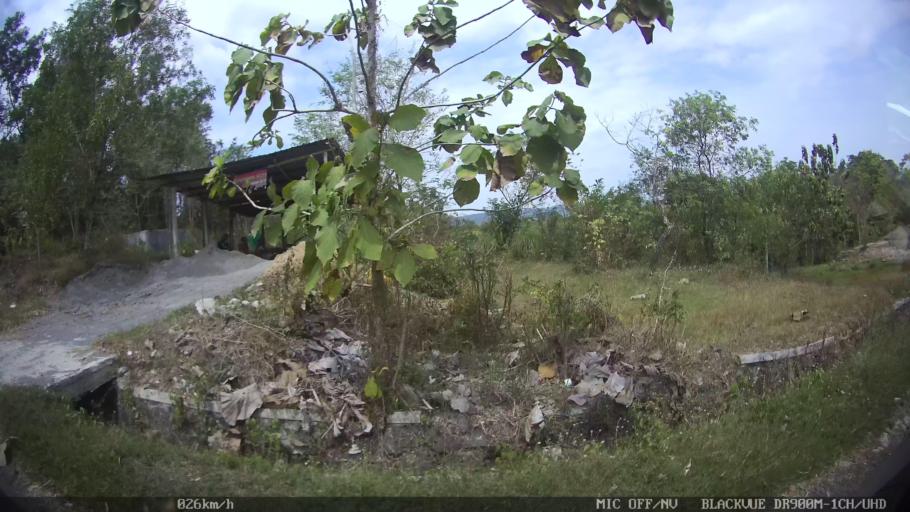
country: ID
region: Central Java
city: Candi Prambanan
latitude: -7.7835
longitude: 110.4914
